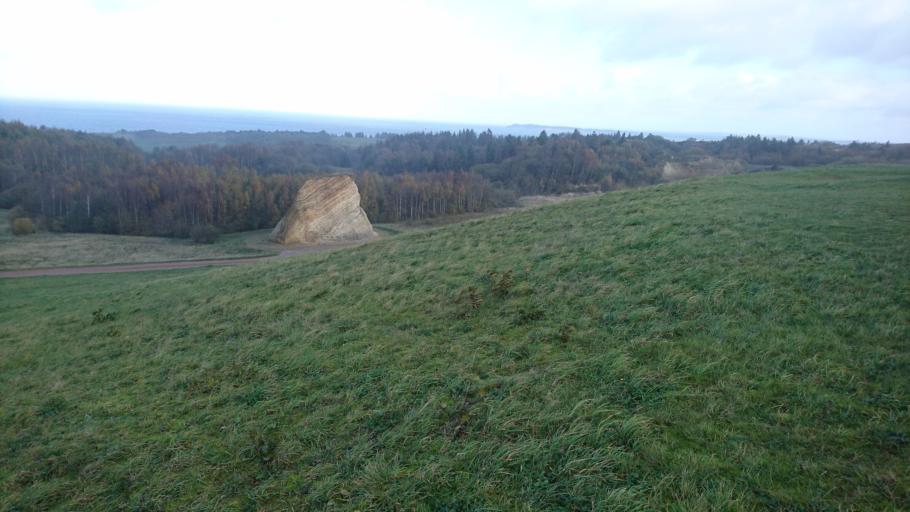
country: DK
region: North Denmark
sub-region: Morso Kommune
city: Nykobing Mors
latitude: 56.8353
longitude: 9.0067
